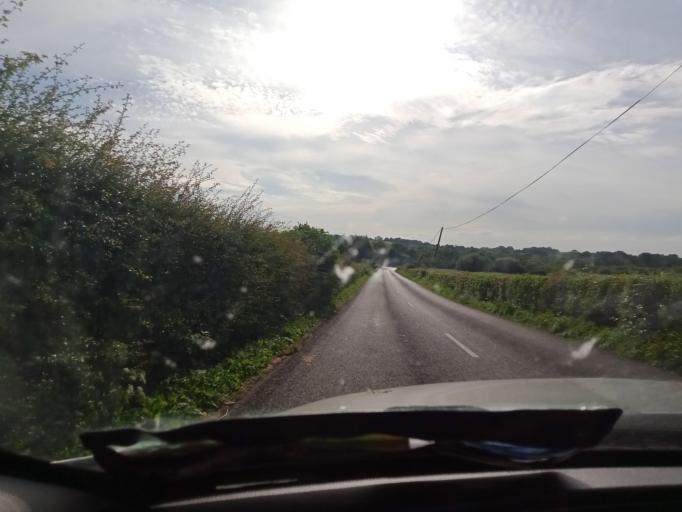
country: IE
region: Leinster
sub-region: An Longfort
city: Granard
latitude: 53.8309
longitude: -7.4362
